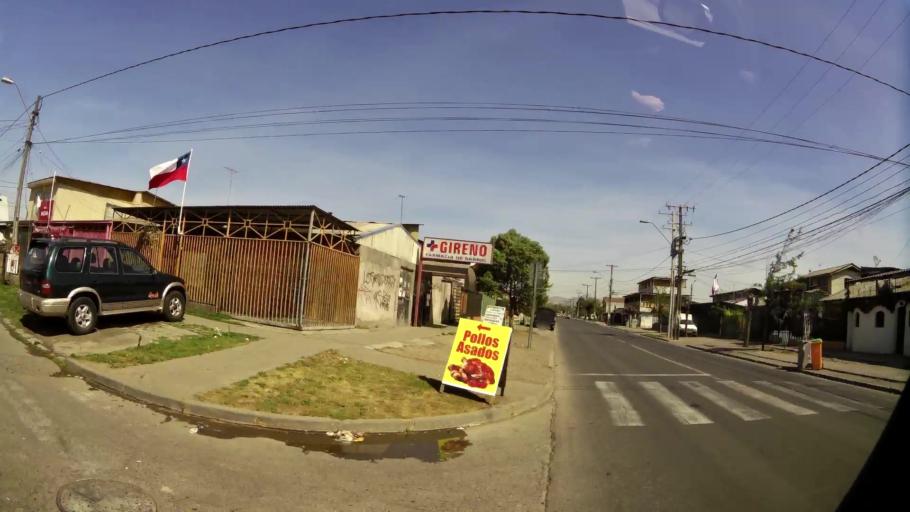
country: CL
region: Santiago Metropolitan
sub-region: Provincia de Maipo
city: San Bernardo
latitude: -33.5277
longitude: -70.7004
